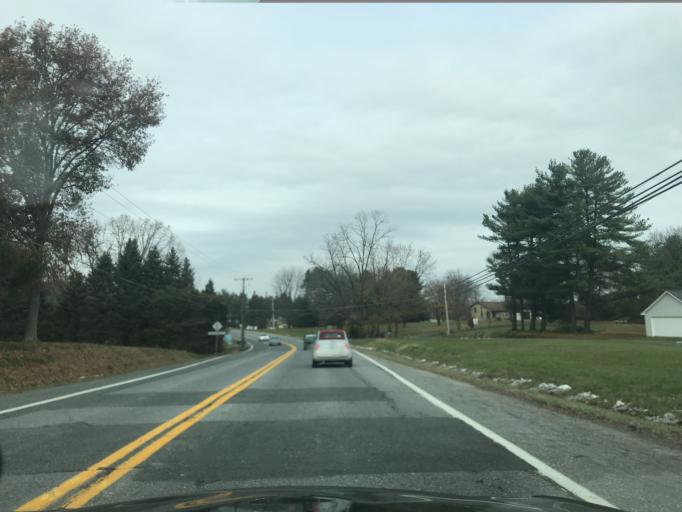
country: US
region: Maryland
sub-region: Harford County
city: Jarrettsville
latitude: 39.6360
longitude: -76.4707
